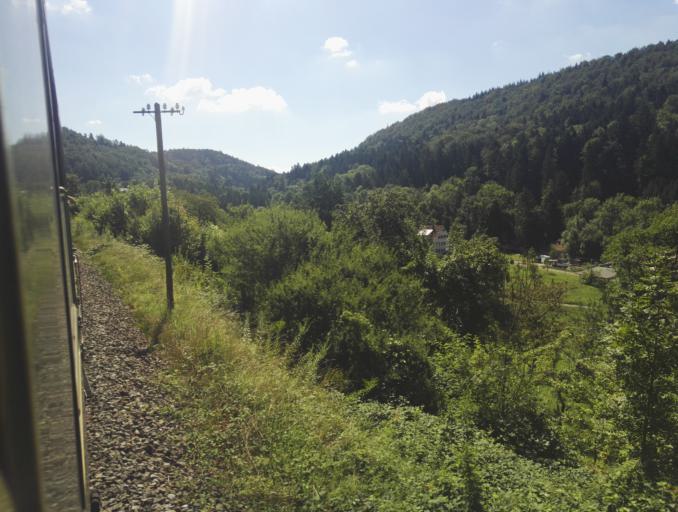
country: DE
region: Baden-Wuerttemberg
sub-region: Regierungsbezirk Stuttgart
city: Althutte
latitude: 48.8974
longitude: 9.5819
